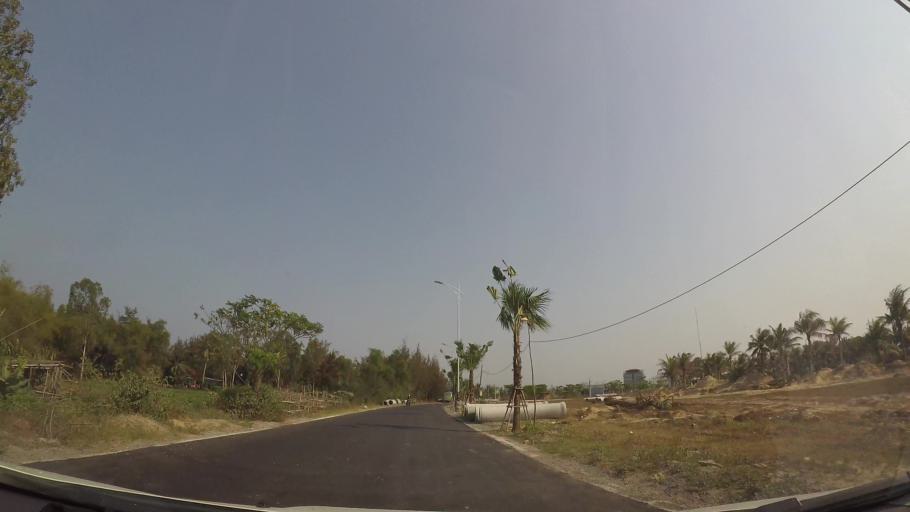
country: VN
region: Da Nang
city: Ngu Hanh Son
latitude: 15.9588
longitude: 108.2813
